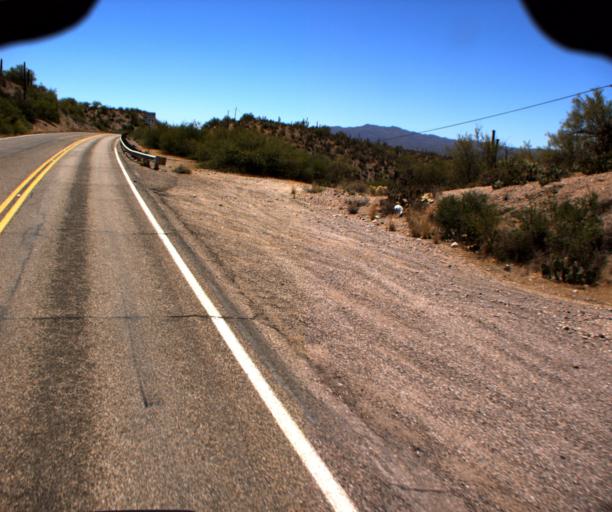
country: US
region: Arizona
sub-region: Pinal County
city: Kearny
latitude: 33.0992
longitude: -110.9346
